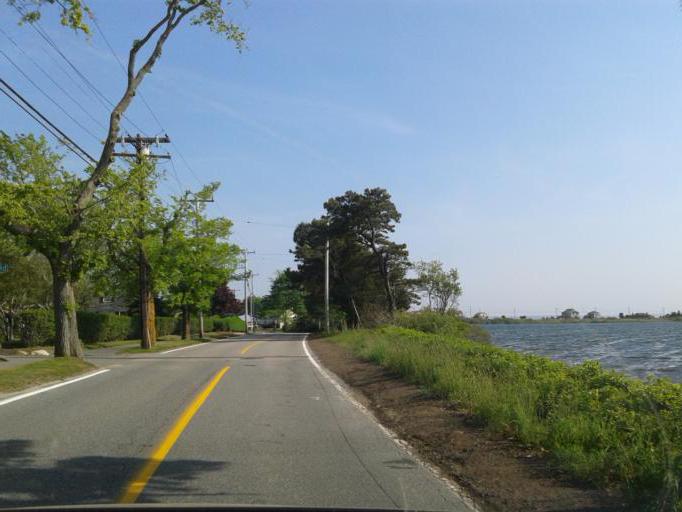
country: US
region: Massachusetts
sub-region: Barnstable County
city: Falmouth
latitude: 41.5451
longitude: -70.6253
